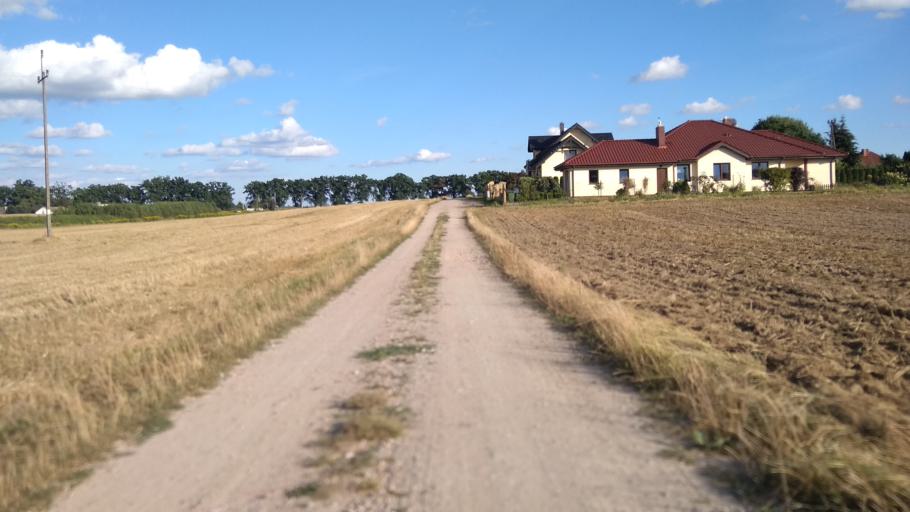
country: PL
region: Kujawsko-Pomorskie
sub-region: Powiat bydgoski
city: Osielsko
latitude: 53.2285
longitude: 18.1259
